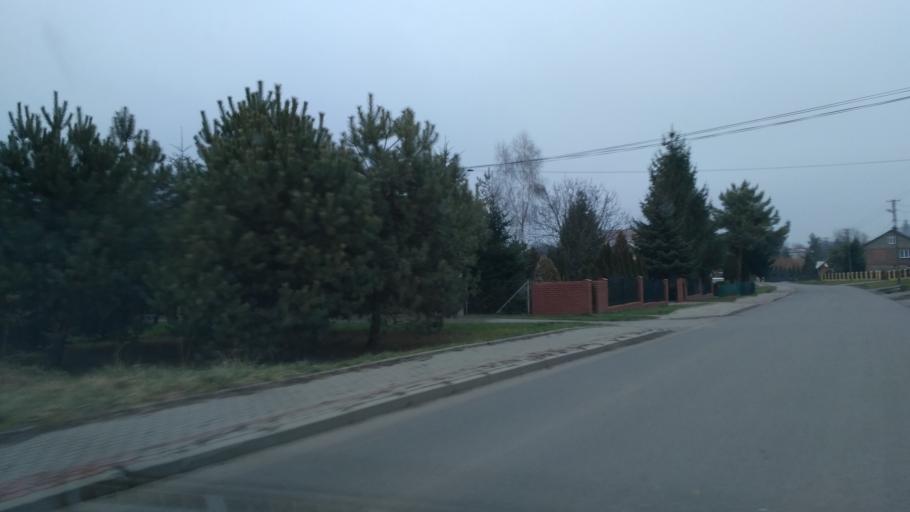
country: PL
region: Subcarpathian Voivodeship
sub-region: Powiat jaroslawski
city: Pawlosiow
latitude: 49.9902
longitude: 22.6405
